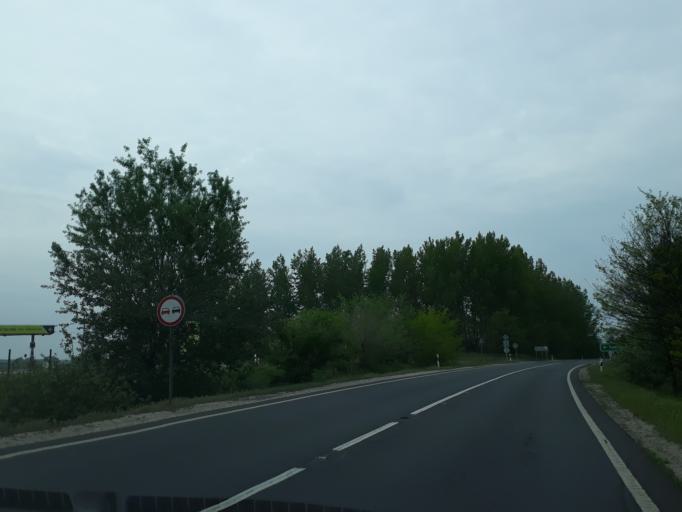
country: HU
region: Szabolcs-Szatmar-Bereg
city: Nyirbogdany
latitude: 48.0607
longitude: 21.9262
